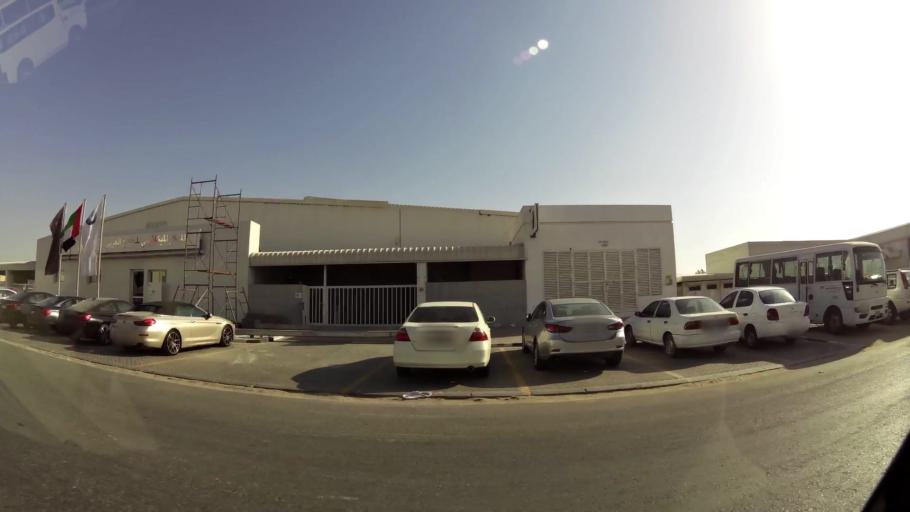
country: AE
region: Dubai
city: Dubai
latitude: 25.1217
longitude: 55.2291
